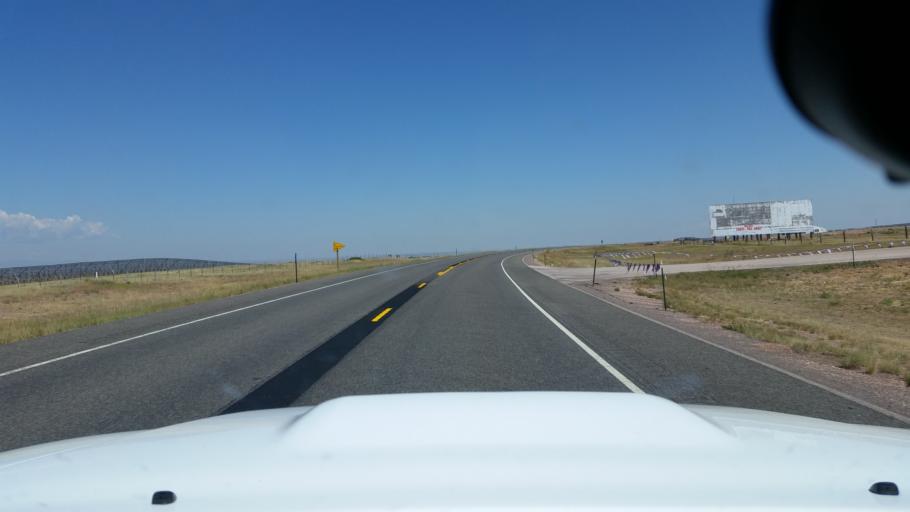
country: US
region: Wyoming
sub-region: Albany County
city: Laramie
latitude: 41.1271
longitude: -105.5504
